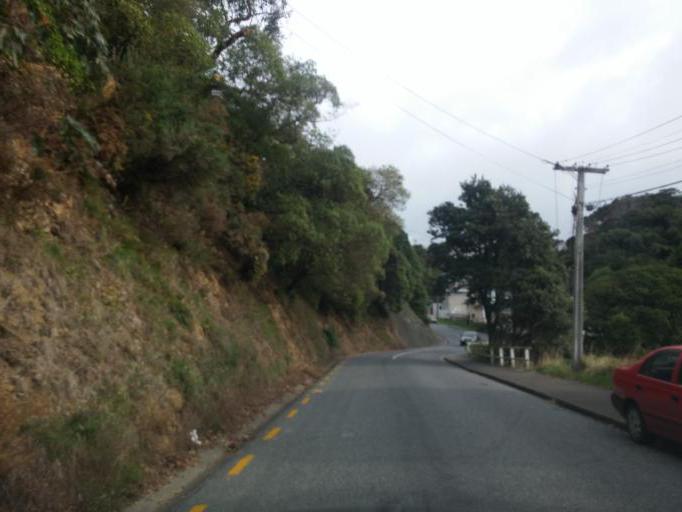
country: NZ
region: Wellington
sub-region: Wellington City
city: Brooklyn
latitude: -41.3134
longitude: 174.7683
